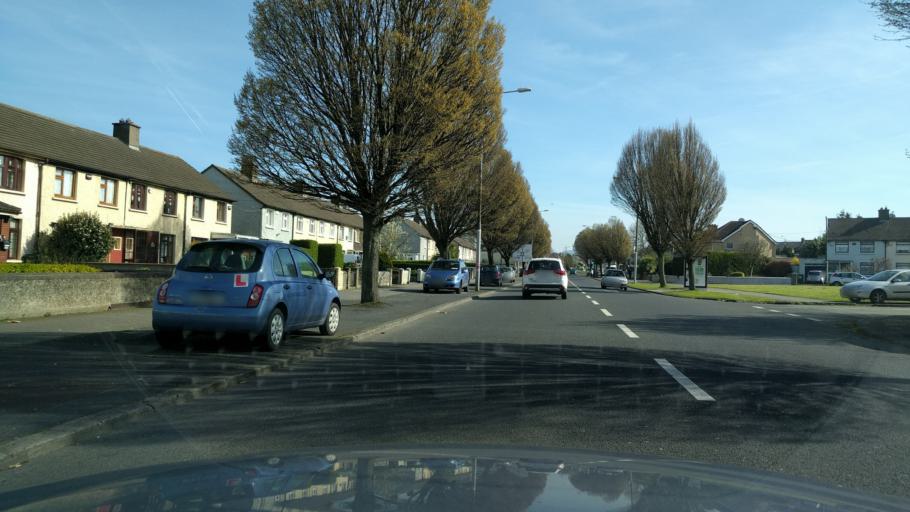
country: IE
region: Leinster
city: Crumlin
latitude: 53.3186
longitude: -6.3354
